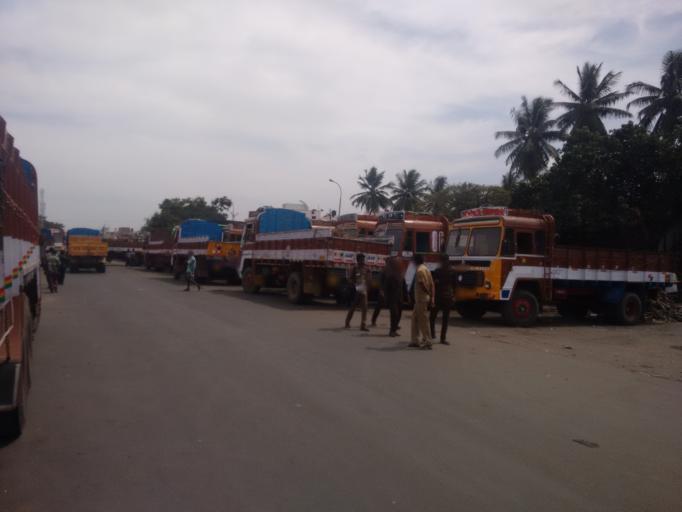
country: IN
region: Tamil Nadu
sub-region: Coimbatore
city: Coimbatore
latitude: 10.9863
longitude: 76.9620
